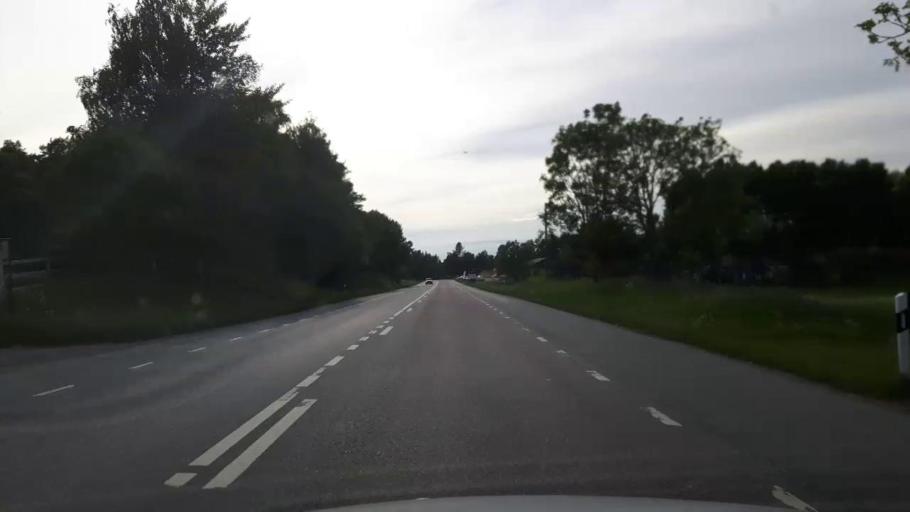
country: SE
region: Uppsala
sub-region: Enkopings Kommun
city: Orsundsbro
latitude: 59.6604
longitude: 17.3274
